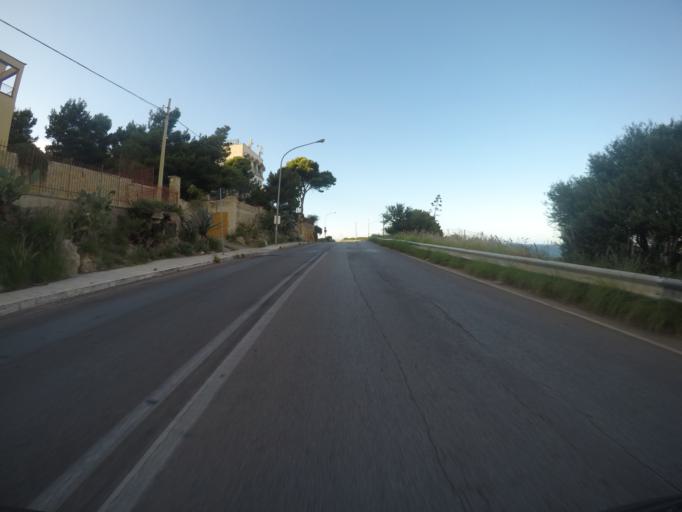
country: IT
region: Sicily
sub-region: Palermo
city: Isola delle Femmine
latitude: 38.2006
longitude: 13.2689
